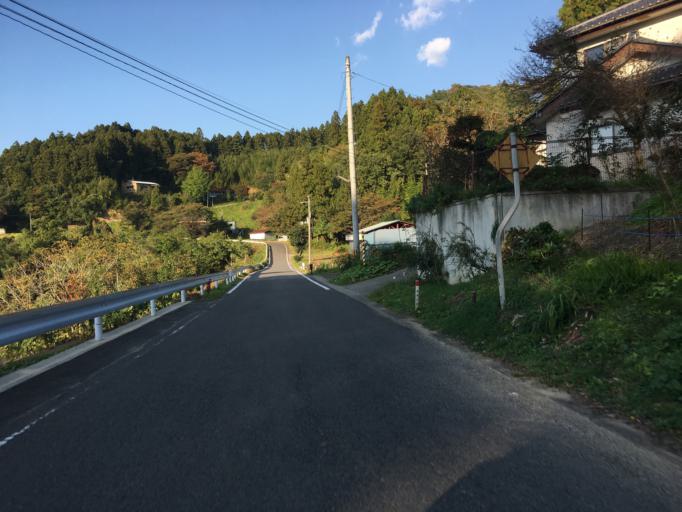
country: JP
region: Fukushima
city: Nihommatsu
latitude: 37.6396
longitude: 140.5725
